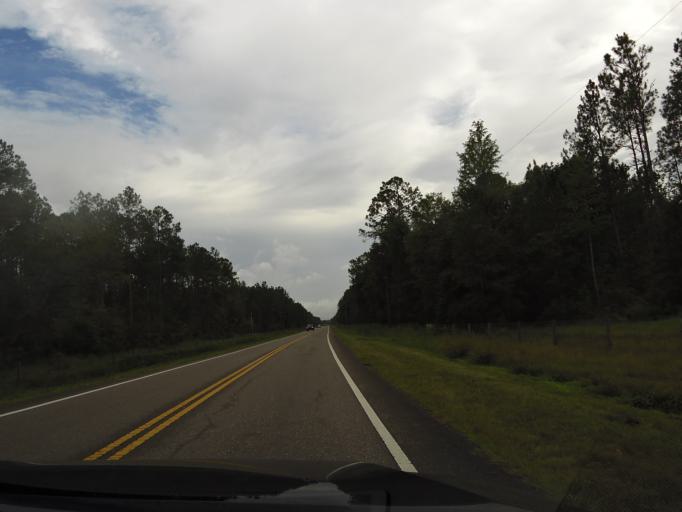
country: US
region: Florida
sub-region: Duval County
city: Baldwin
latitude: 30.3590
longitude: -81.9163
